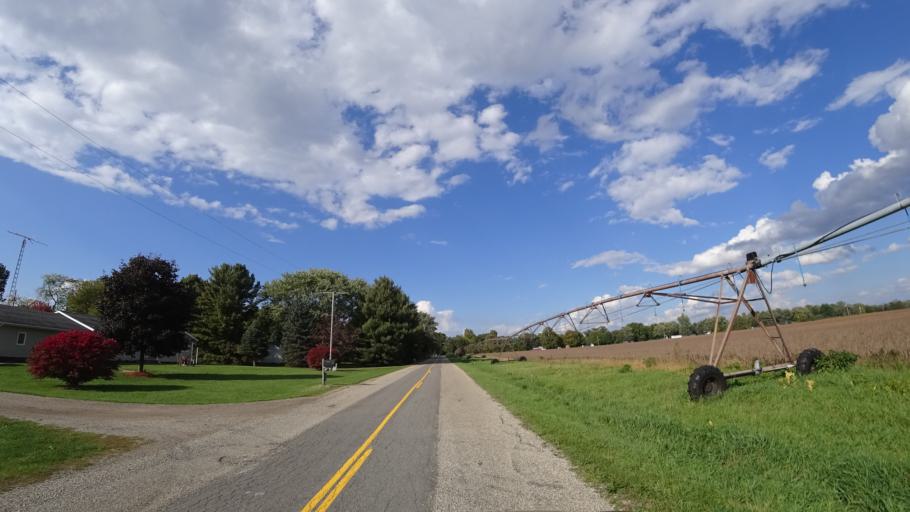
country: US
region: Michigan
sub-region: Saint Joseph County
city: Three Rivers
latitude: 41.9437
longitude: -85.6042
